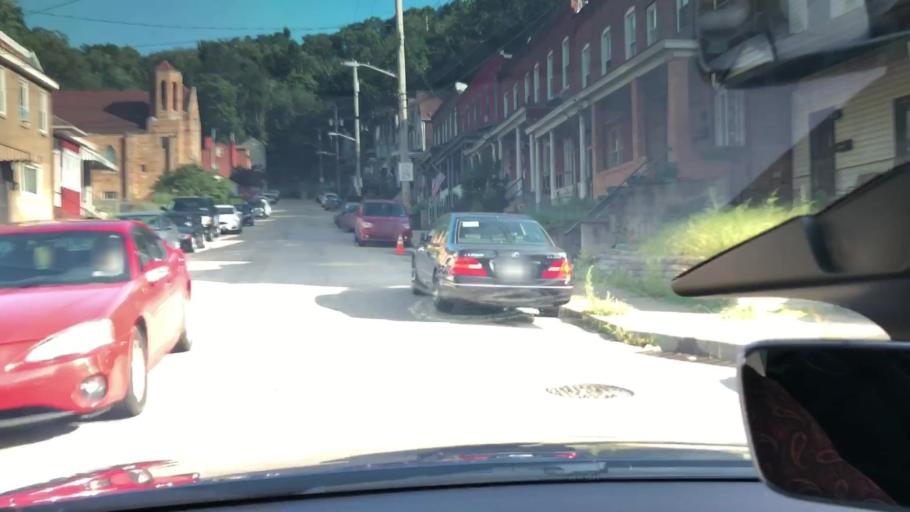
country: US
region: Pennsylvania
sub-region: Allegheny County
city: Etna
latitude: 40.4846
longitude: -79.9457
